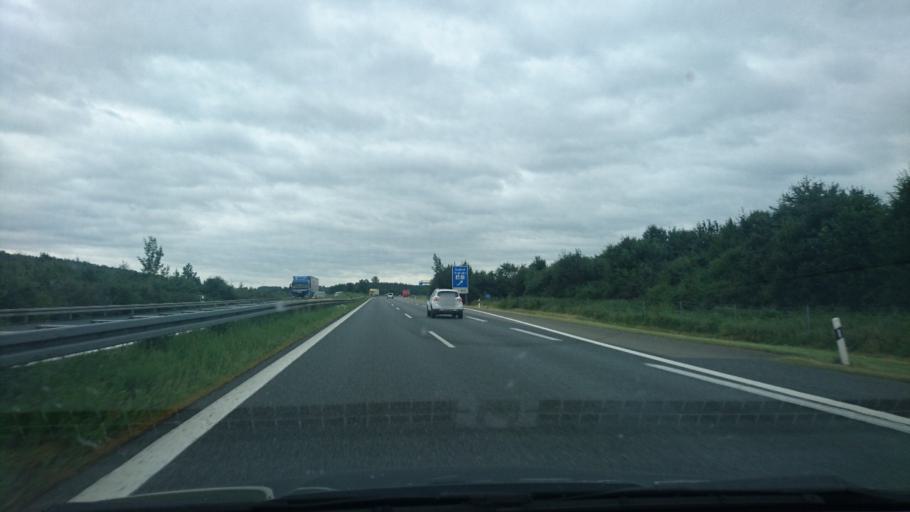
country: DE
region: Saxony
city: Theuma
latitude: 50.4711
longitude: 12.1849
